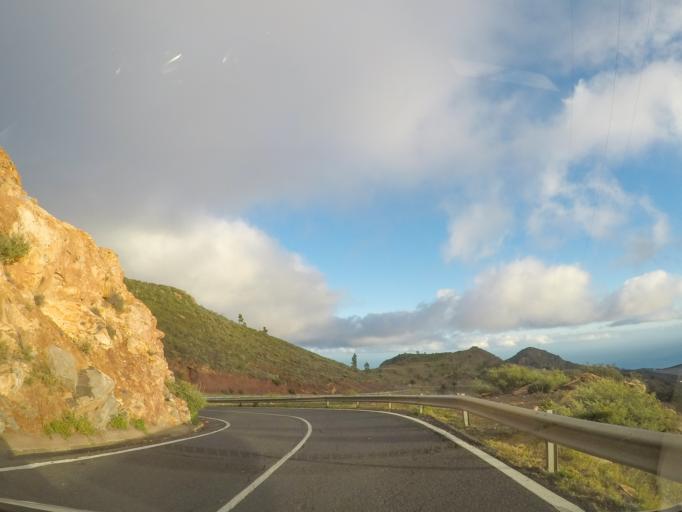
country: ES
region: Canary Islands
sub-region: Provincia de Santa Cruz de Tenerife
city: Alajero
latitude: 28.0864
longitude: -17.2481
